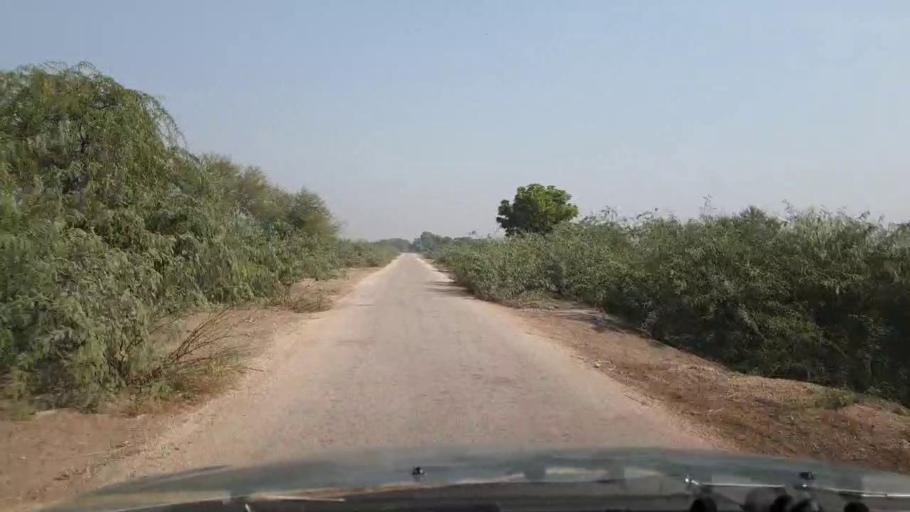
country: PK
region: Sindh
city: Tando Jam
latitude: 25.3071
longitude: 68.5381
